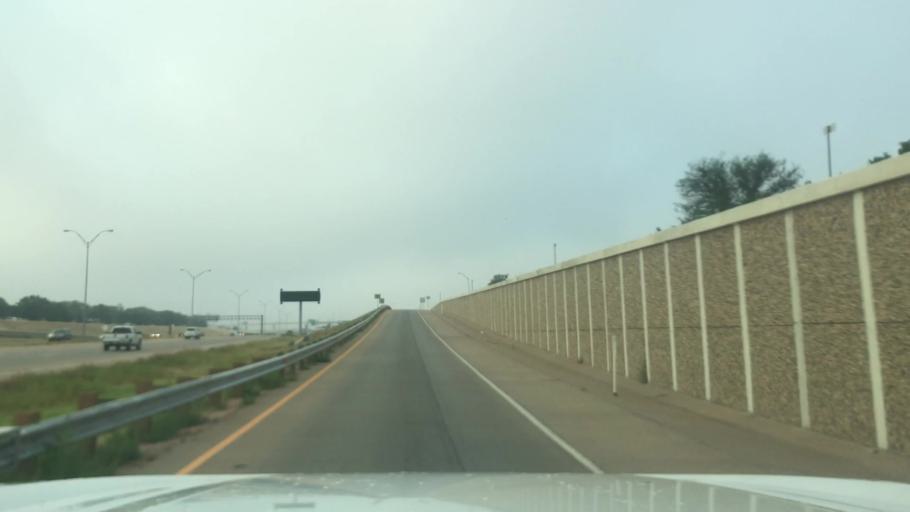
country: US
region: Texas
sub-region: Lubbock County
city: Lubbock
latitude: 33.5471
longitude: -101.8454
